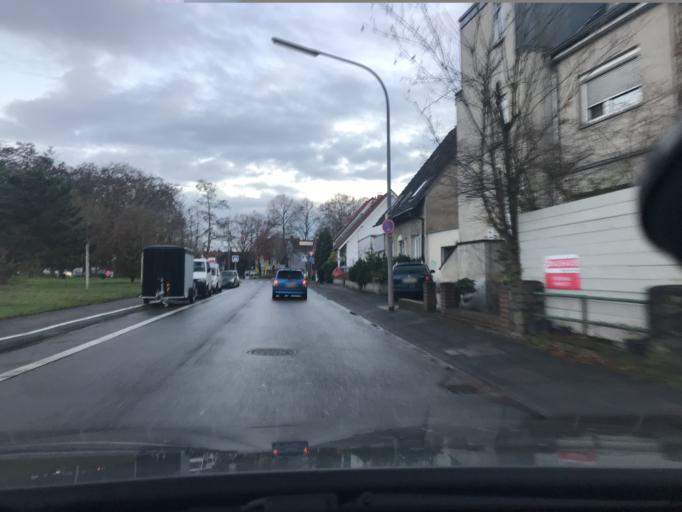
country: DE
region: North Rhine-Westphalia
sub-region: Regierungsbezirk Koln
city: Merheim
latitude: 50.9689
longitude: 7.0665
